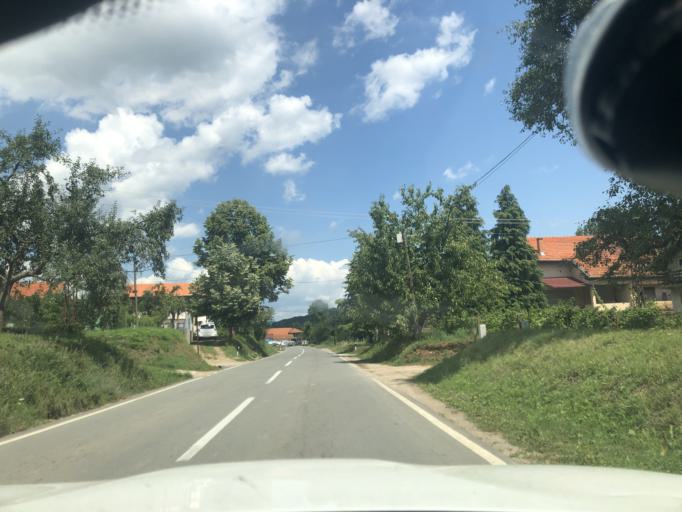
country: RS
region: Central Serbia
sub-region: Jablanicki Okrug
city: Medvega
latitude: 42.8556
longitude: 21.5906
